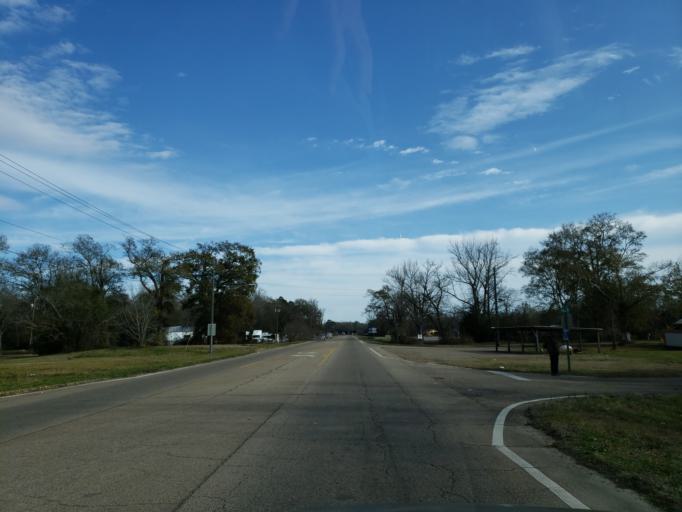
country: US
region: Mississippi
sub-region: Forrest County
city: Hattiesburg
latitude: 31.3430
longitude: -89.2946
